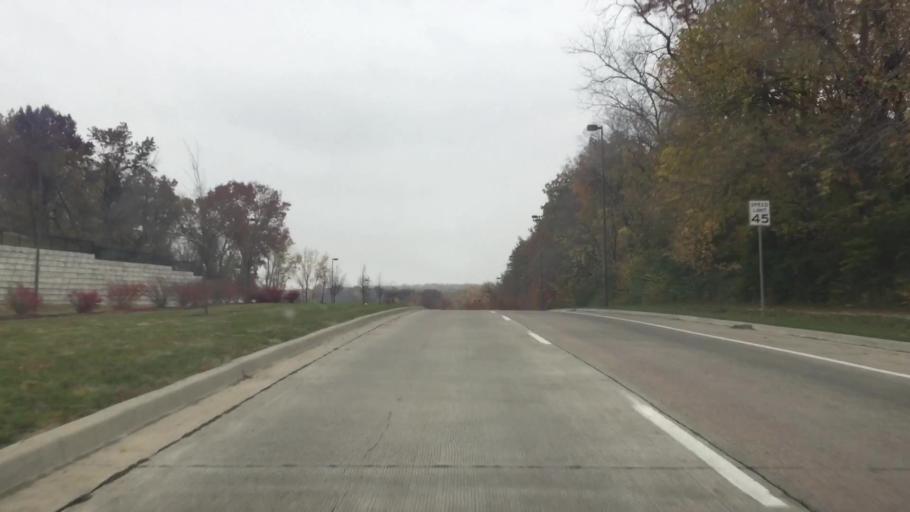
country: US
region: Missouri
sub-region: Clay County
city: North Kansas City
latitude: 39.1575
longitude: -94.5343
